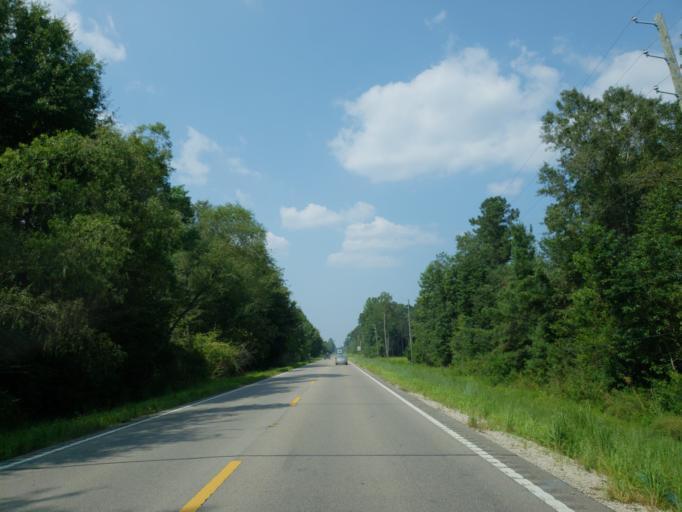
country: US
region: Mississippi
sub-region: Forrest County
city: Glendale
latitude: 31.4679
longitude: -89.2836
